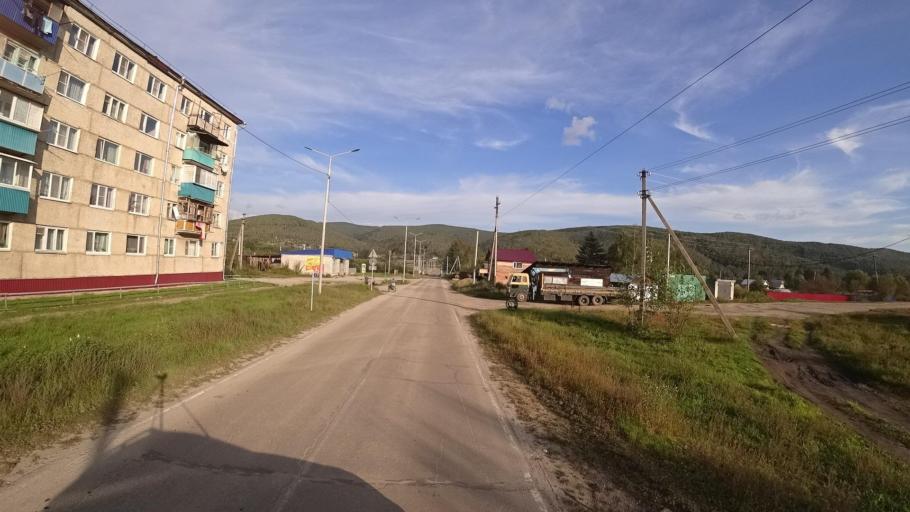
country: RU
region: Jewish Autonomous Oblast
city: Kul'dur
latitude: 49.2012
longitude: 131.6263
